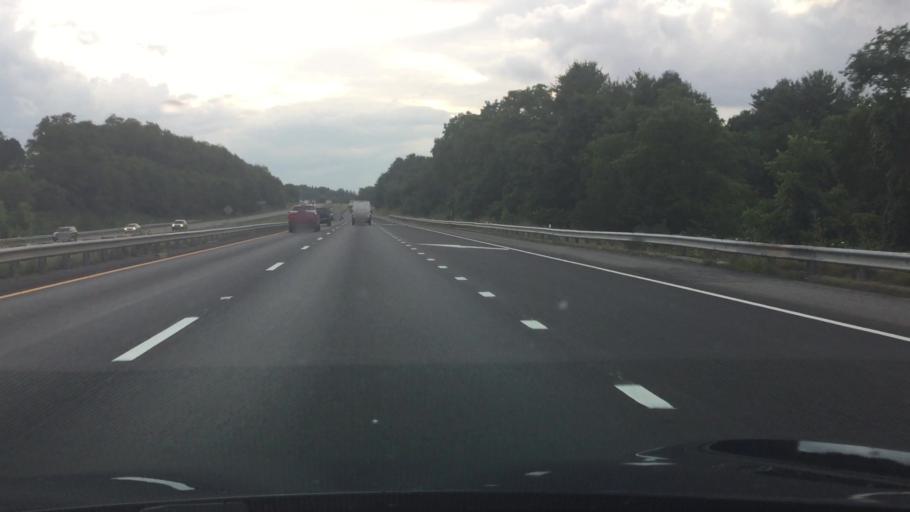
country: US
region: Virginia
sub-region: Montgomery County
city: Christiansburg
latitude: 37.1162
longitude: -80.4253
